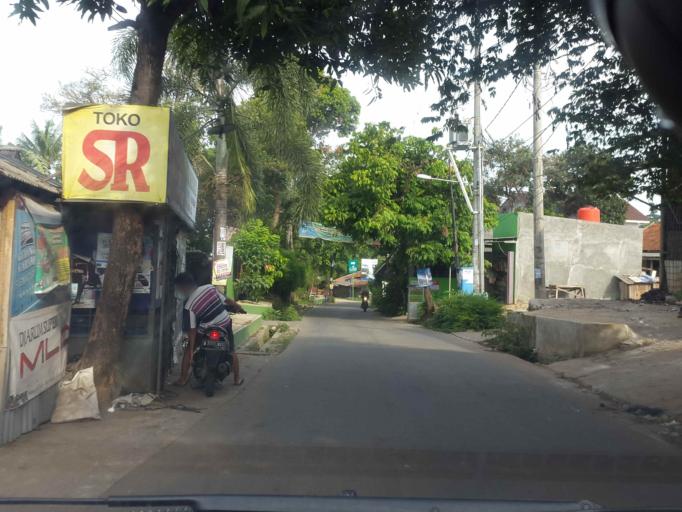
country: ID
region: West Java
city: Serpong
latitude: -6.2794
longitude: 106.6735
